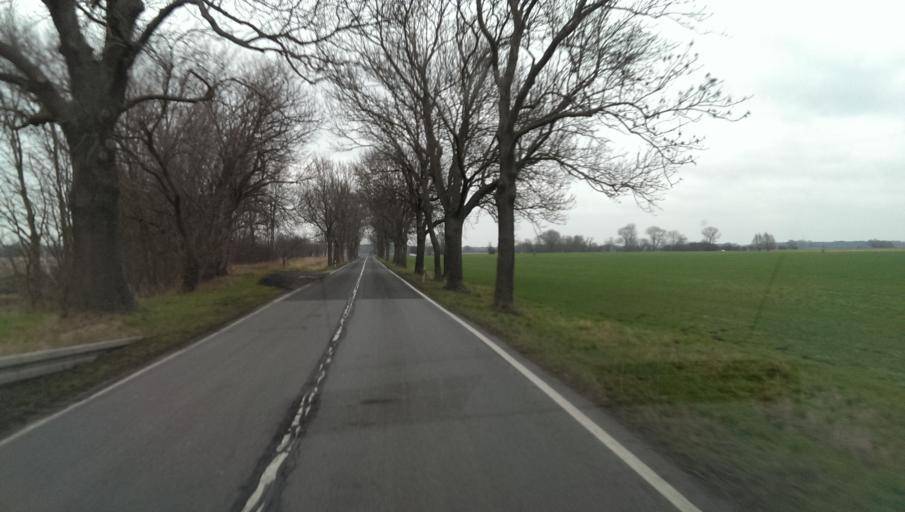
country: DE
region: Brandenburg
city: Rangsdorf
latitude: 52.2819
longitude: 13.3702
